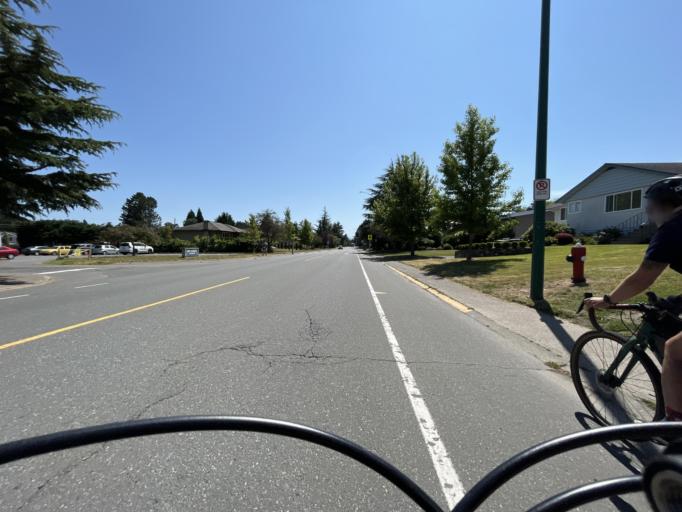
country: CA
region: British Columbia
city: Oak Bay
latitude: 48.4535
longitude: -123.3151
